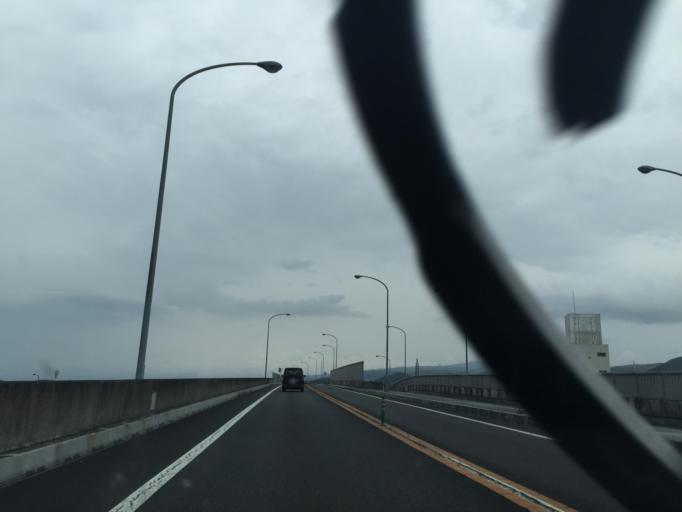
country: JP
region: Shizuoka
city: Mishima
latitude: 35.0084
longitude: 138.9389
